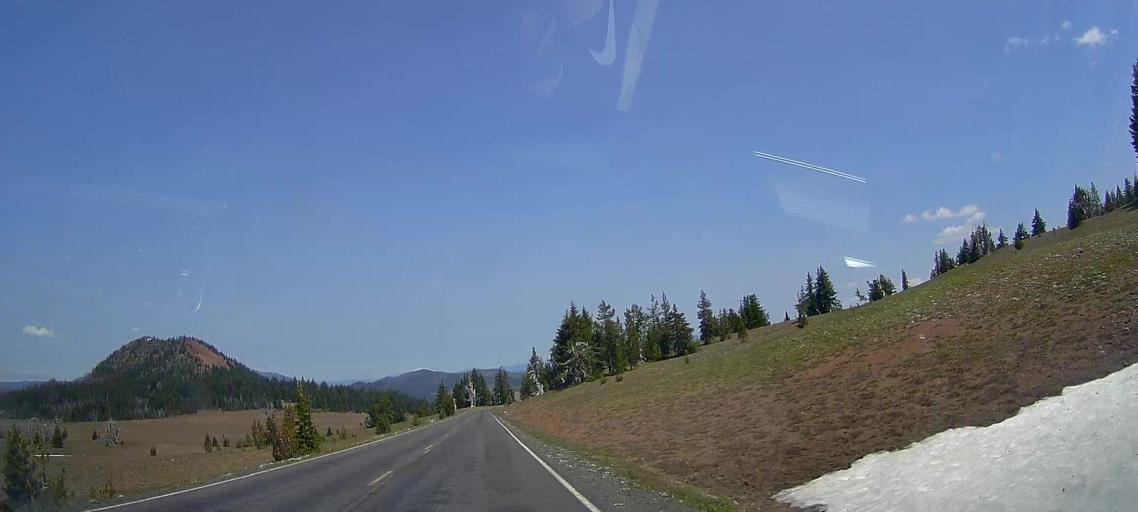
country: US
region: Oregon
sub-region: Jackson County
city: Shady Cove
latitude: 42.9798
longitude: -122.1528
